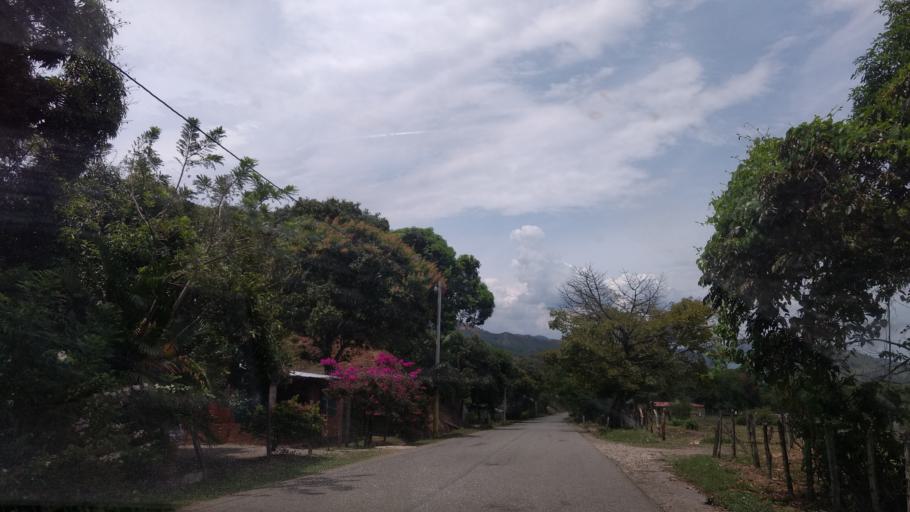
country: CO
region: Cauca
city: Buenos Aires
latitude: 3.0582
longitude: -76.6587
